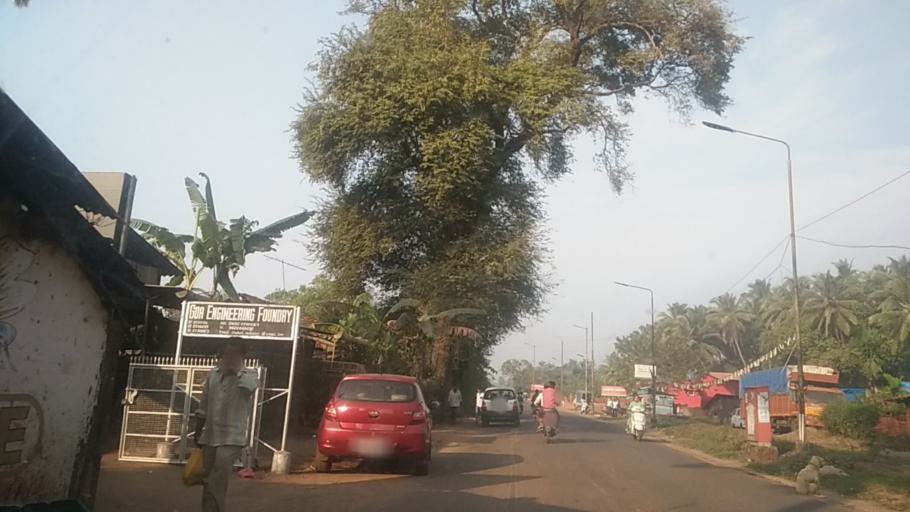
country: IN
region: Goa
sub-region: South Goa
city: Madgaon
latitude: 15.2693
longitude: 73.9547
